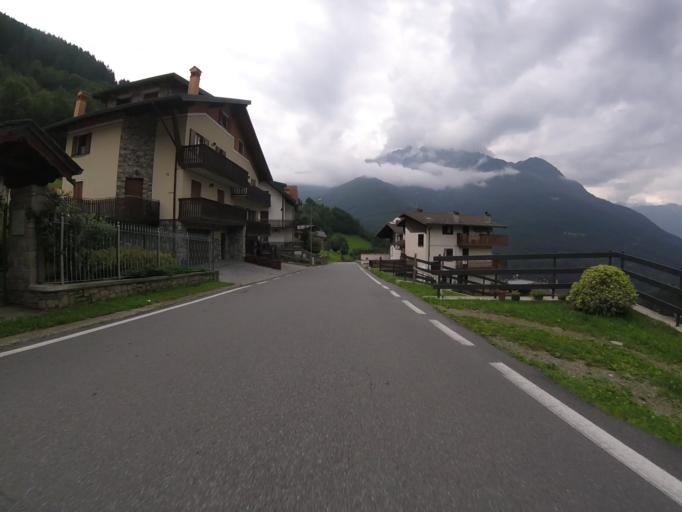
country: IT
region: Lombardy
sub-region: Provincia di Brescia
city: Monno
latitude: 46.2134
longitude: 10.3405
